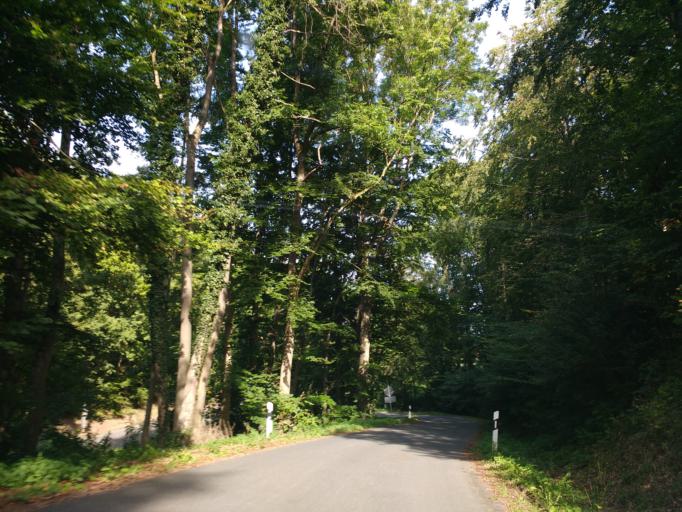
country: DE
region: Hesse
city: Witzenhausen
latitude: 51.4017
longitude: 9.8335
